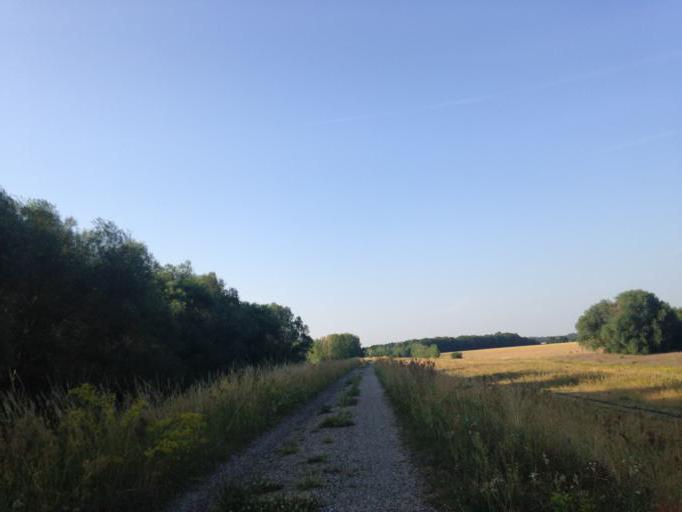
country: AT
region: Lower Austria
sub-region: Politischer Bezirk Ganserndorf
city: Angern an der March
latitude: 48.3869
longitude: 16.8553
